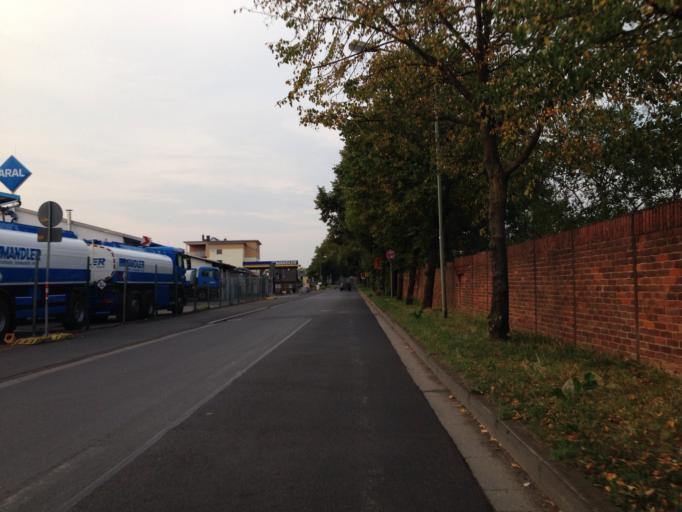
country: DE
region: Hesse
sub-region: Regierungsbezirk Giessen
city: Giessen
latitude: 50.5758
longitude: 8.6566
